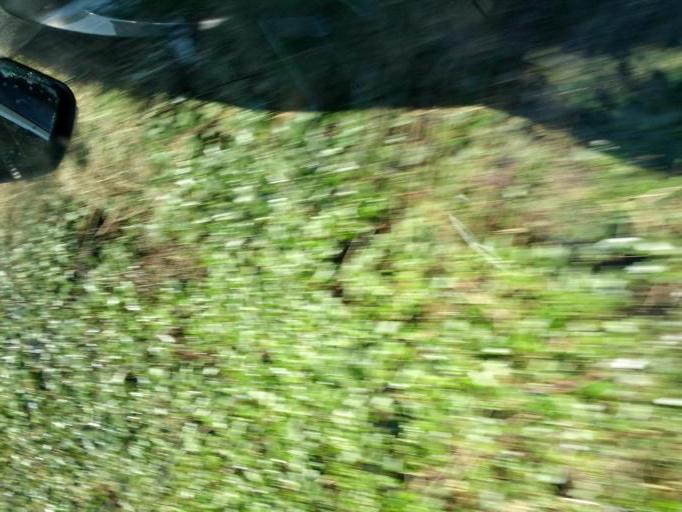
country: IE
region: Connaught
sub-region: County Galway
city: Athenry
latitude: 53.1895
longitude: -8.7890
